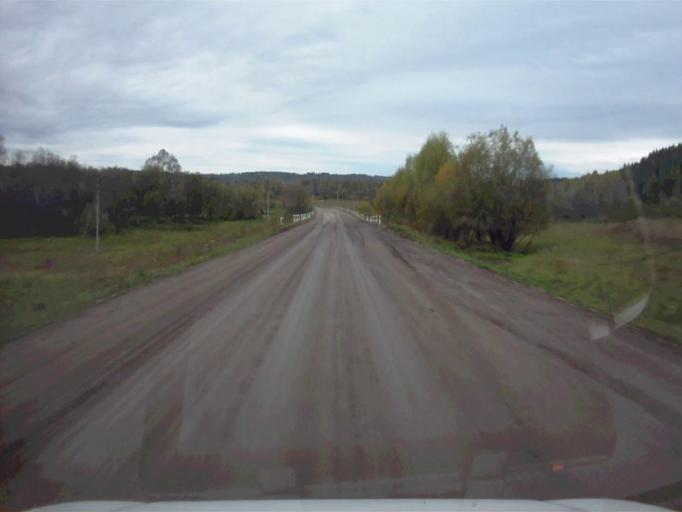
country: RU
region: Chelyabinsk
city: Nyazepetrovsk
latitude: 56.1239
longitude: 59.3564
